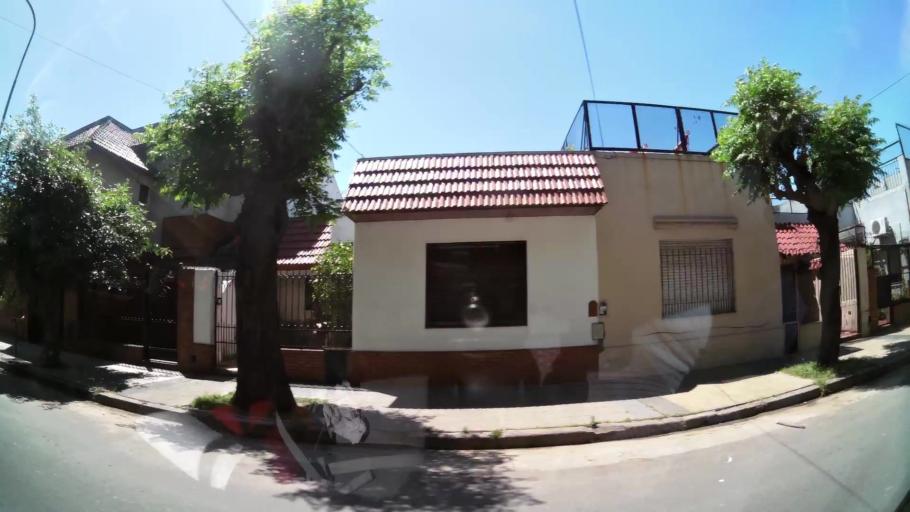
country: AR
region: Buenos Aires F.D.
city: Buenos Aires
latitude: -34.6435
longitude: -58.4094
